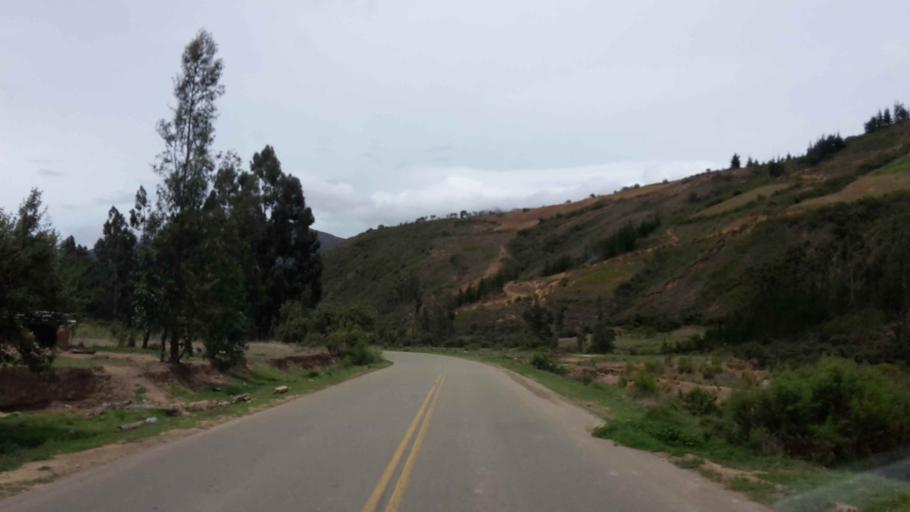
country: BO
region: Cochabamba
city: Totora
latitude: -17.6689
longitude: -65.2220
